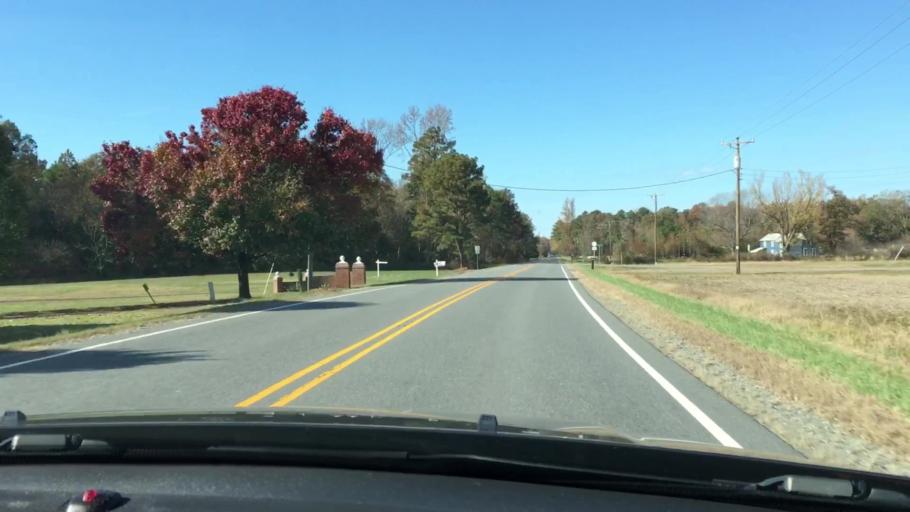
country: US
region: Virginia
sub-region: King William County
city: King William
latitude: 37.6606
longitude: -76.9592
